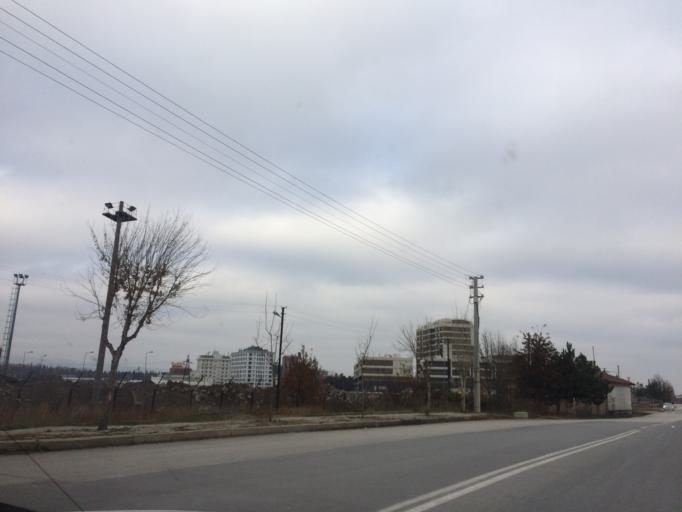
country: TR
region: Eskisehir
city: Eskisehir
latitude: 39.7799
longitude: 30.4921
